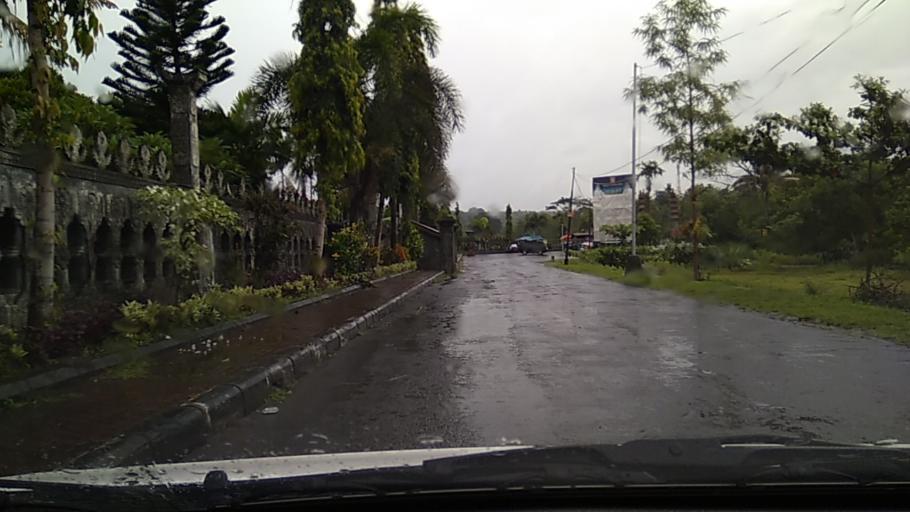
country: ID
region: Bali
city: Banjar Danginsema
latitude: -8.4648
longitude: 115.6319
